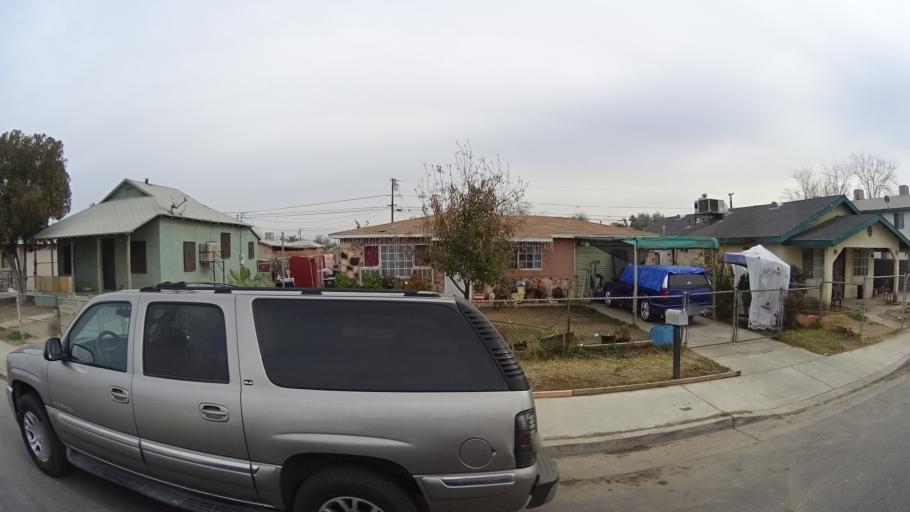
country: US
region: California
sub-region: Kern County
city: Bakersfield
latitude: 35.3582
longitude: -118.9897
